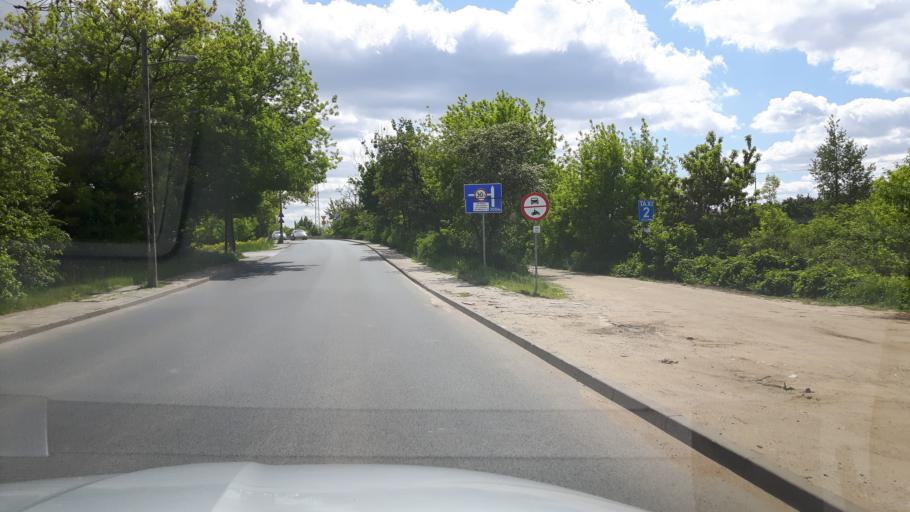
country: PL
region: Masovian Voivodeship
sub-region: Warszawa
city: Targowek
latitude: 52.3288
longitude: 21.0316
